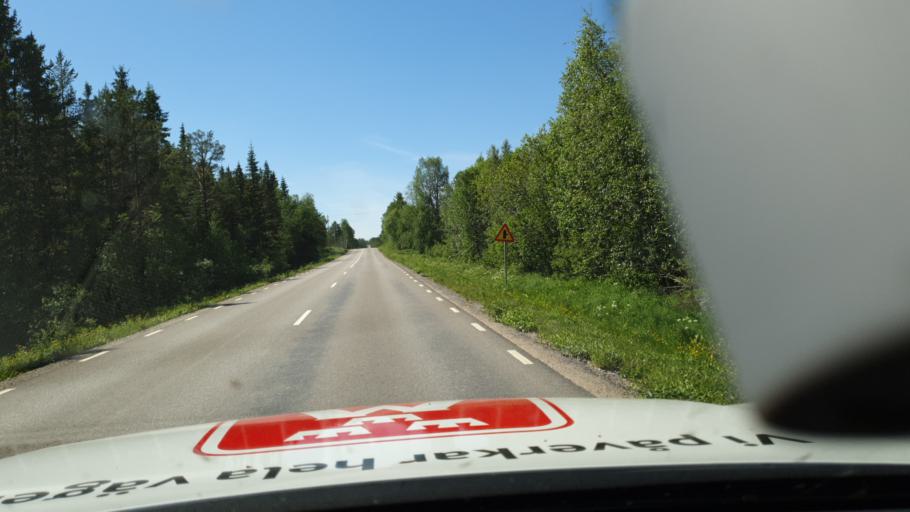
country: SE
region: Jaemtland
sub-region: Harjedalens Kommun
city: Sveg
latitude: 62.1060
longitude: 13.4785
